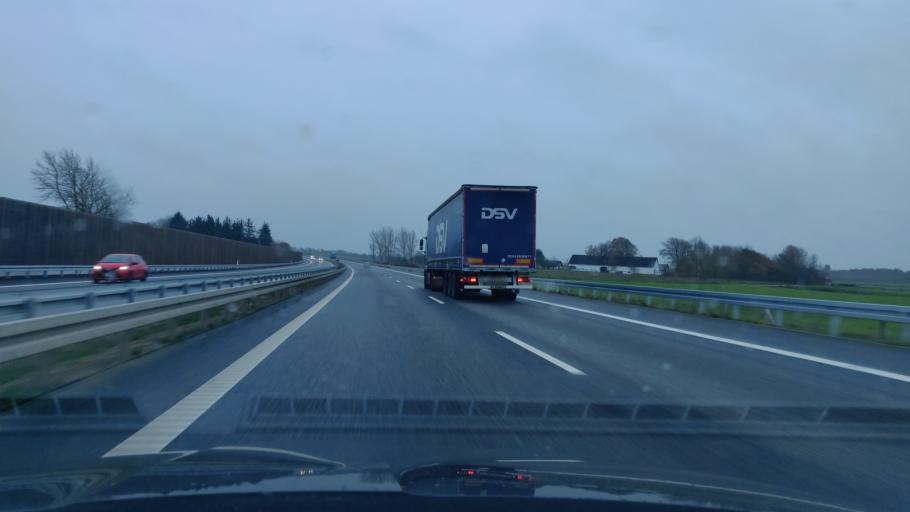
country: DK
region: Central Jutland
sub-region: Herning Kommune
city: Avlum
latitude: 56.2373
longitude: 8.8068
